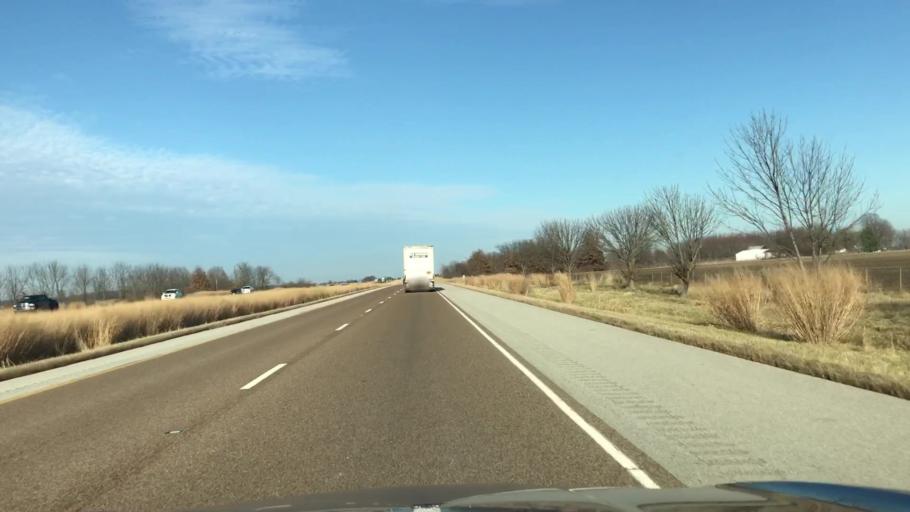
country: US
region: Illinois
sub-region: Macoupin County
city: Mount Olive
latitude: 39.1305
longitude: -89.7109
